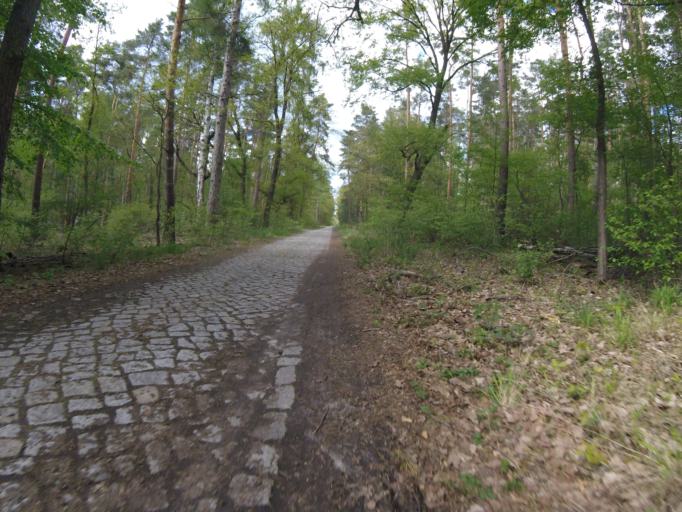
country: DE
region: Brandenburg
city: Schwerin
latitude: 52.1778
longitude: 13.5969
